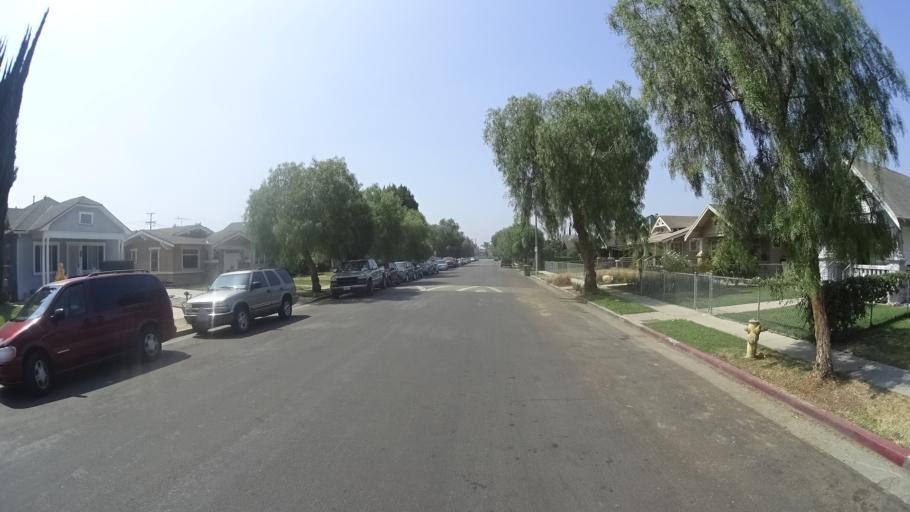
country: US
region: California
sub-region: Los Angeles County
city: View Park-Windsor Hills
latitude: 34.0217
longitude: -118.3202
